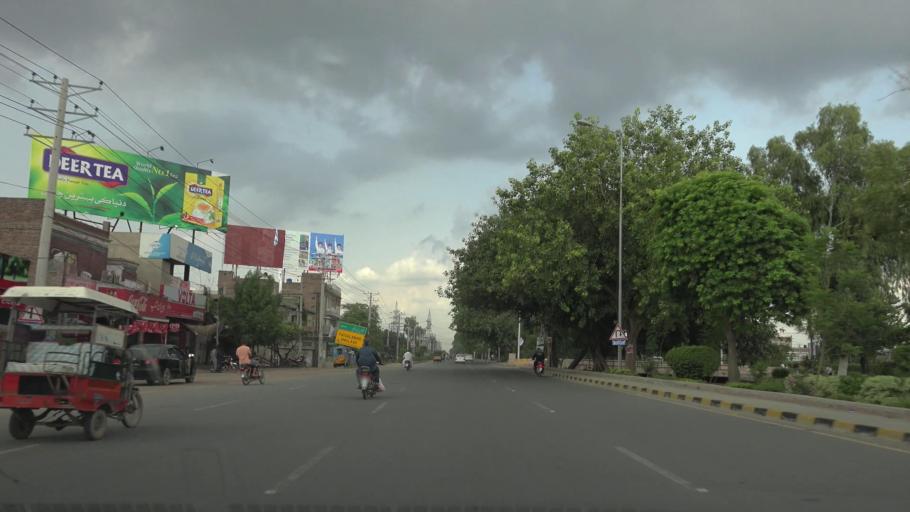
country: PK
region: Punjab
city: Faisalabad
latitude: 31.4297
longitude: 73.1193
